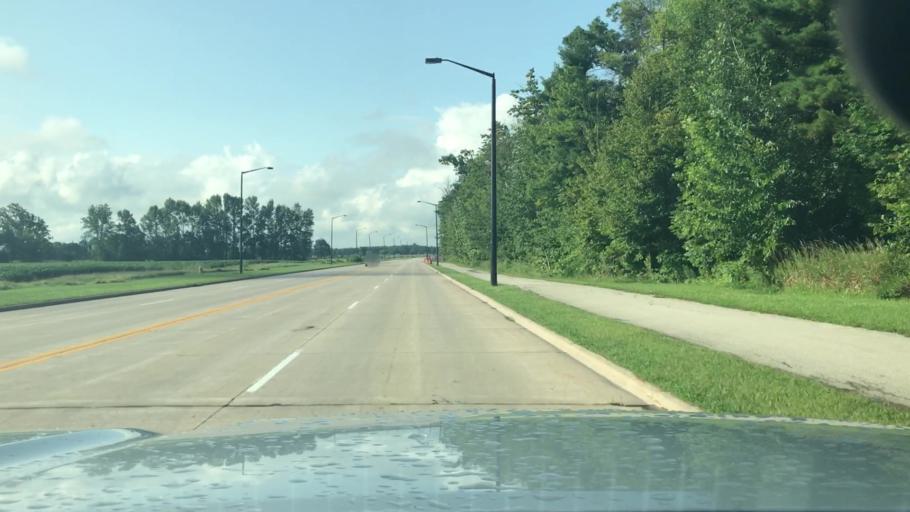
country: US
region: Wisconsin
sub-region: Brown County
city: Bellevue
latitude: 44.4757
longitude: -87.9173
